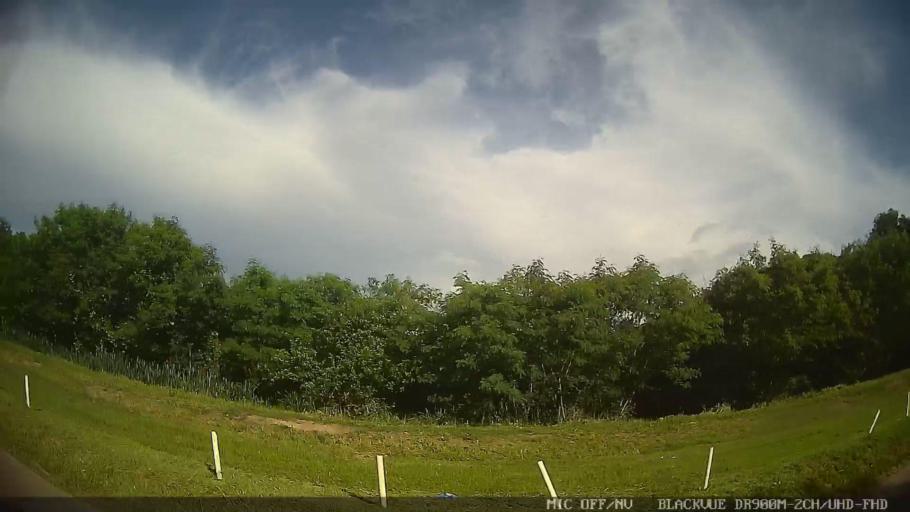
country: BR
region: Sao Paulo
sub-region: Tiete
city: Tiete
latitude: -23.1007
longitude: -47.6914
